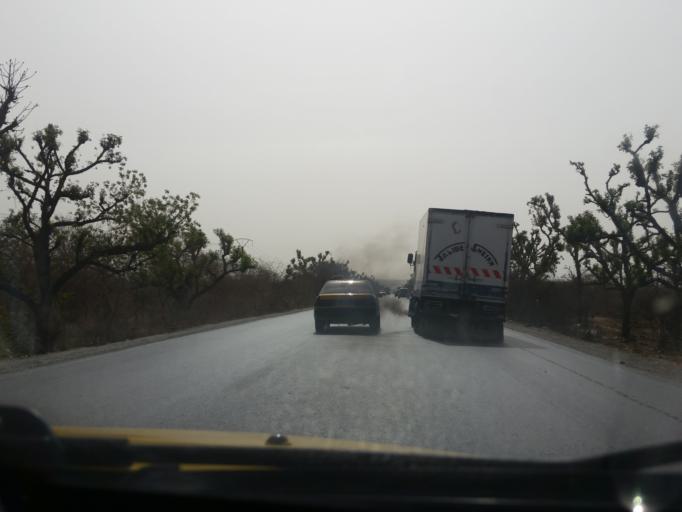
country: SN
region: Thies
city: Pout
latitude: 14.7628
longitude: -17.0261
